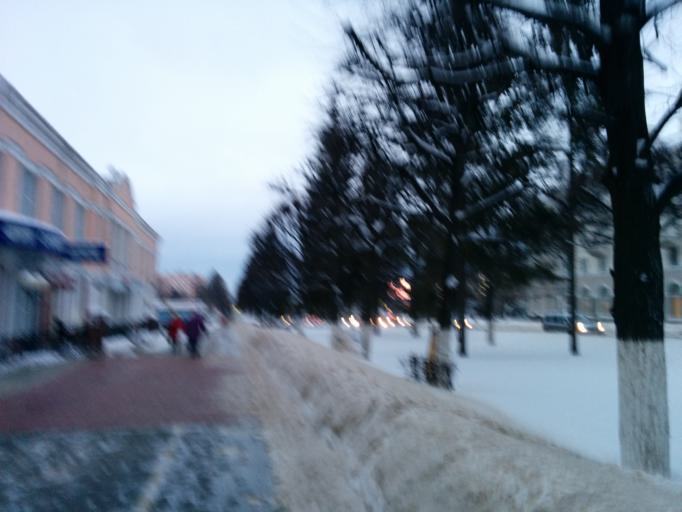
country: RU
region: Chuvashia
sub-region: Cheboksarskiy Rayon
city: Cheboksary
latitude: 56.1330
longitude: 47.2460
